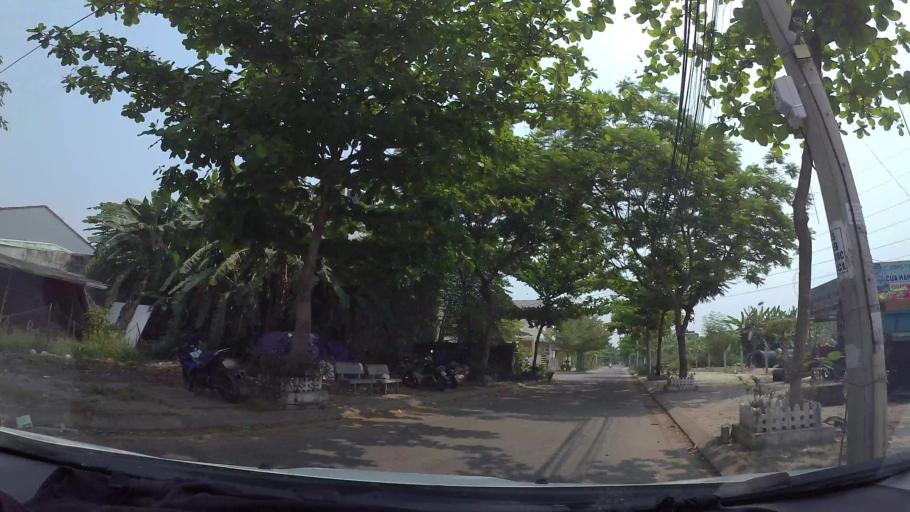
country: VN
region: Da Nang
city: Cam Le
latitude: 16.0021
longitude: 108.2105
